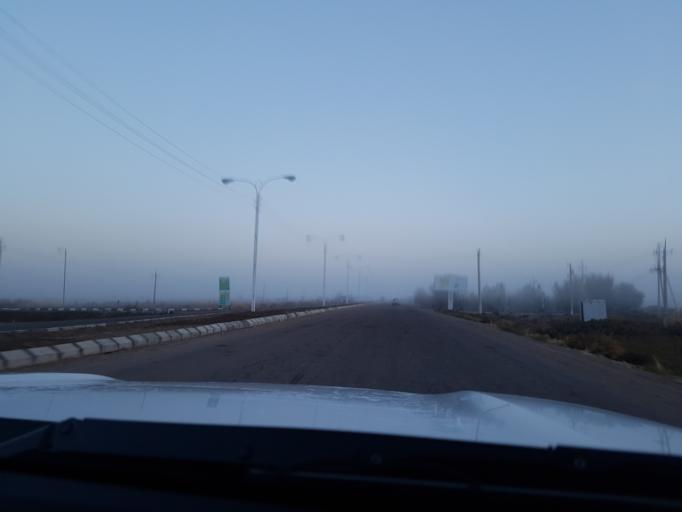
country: TM
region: Dasoguz
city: Koeneuergench
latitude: 41.7359
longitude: 58.6866
